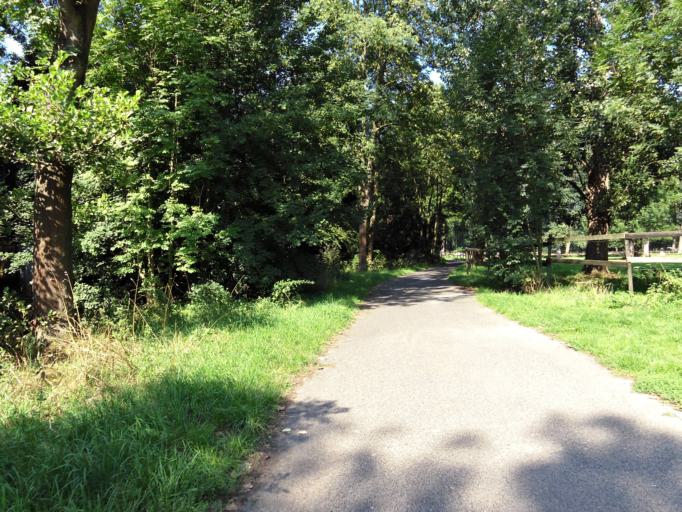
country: DE
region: North Rhine-Westphalia
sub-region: Regierungsbezirk Koln
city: Linnich
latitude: 51.0085
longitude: 6.2400
